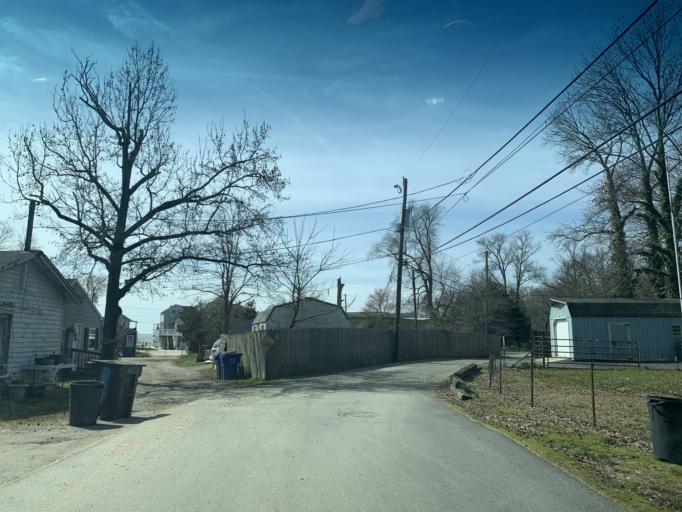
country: US
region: Maryland
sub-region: Cecil County
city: Charlestown
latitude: 39.5697
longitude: -75.9822
